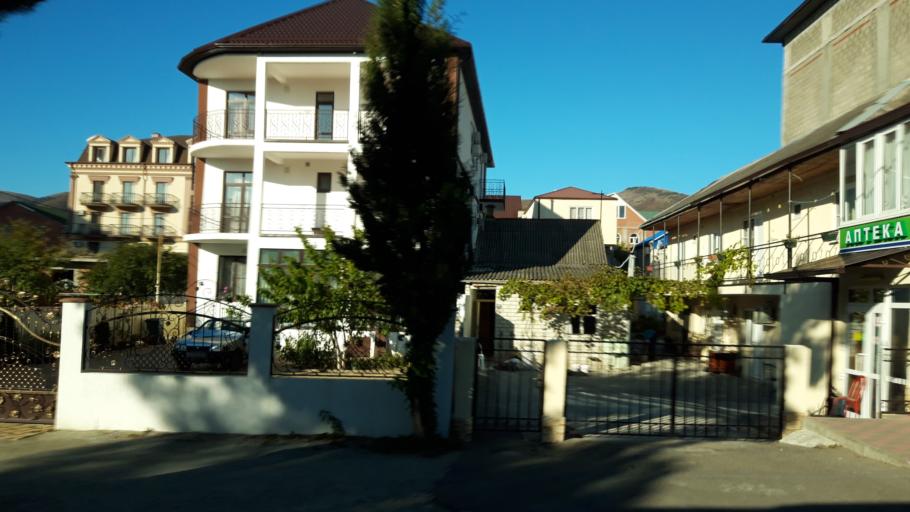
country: RU
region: Krasnodarskiy
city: Kabardinka
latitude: 44.6510
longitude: 37.9410
